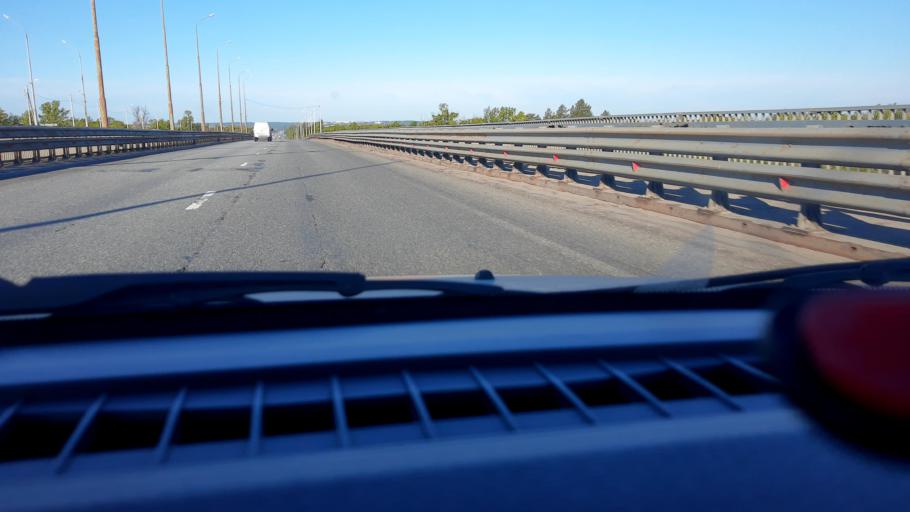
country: RU
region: Vladimir
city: Galitsy
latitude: 56.2232
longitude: 42.7789
